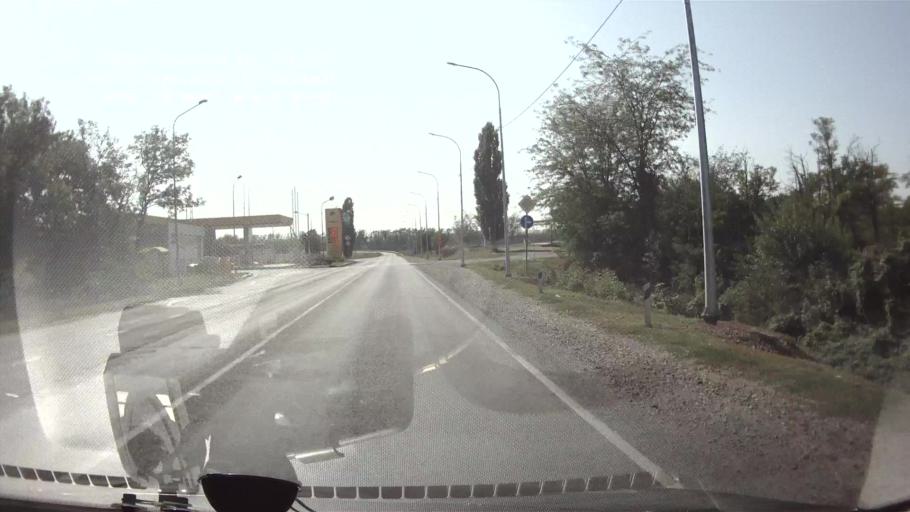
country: RU
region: Krasnodarskiy
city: Dmitriyevskaya
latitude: 45.7093
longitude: 40.7255
